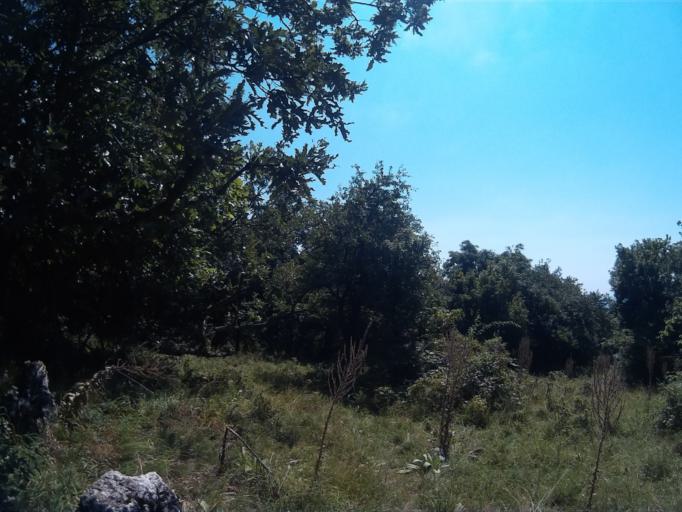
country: HU
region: Veszprem
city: Zirc
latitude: 47.1796
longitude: 17.8607
